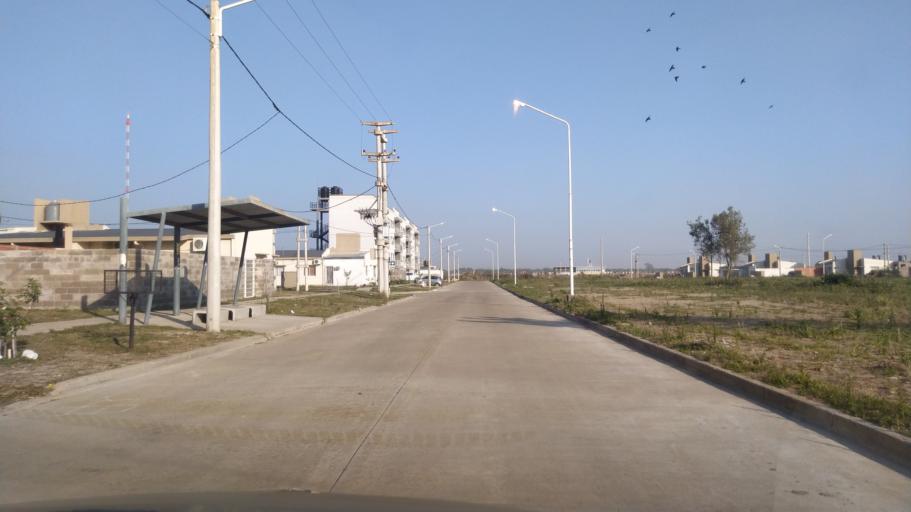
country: AR
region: Corrientes
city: Corrientes
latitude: -27.5275
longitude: -58.8060
